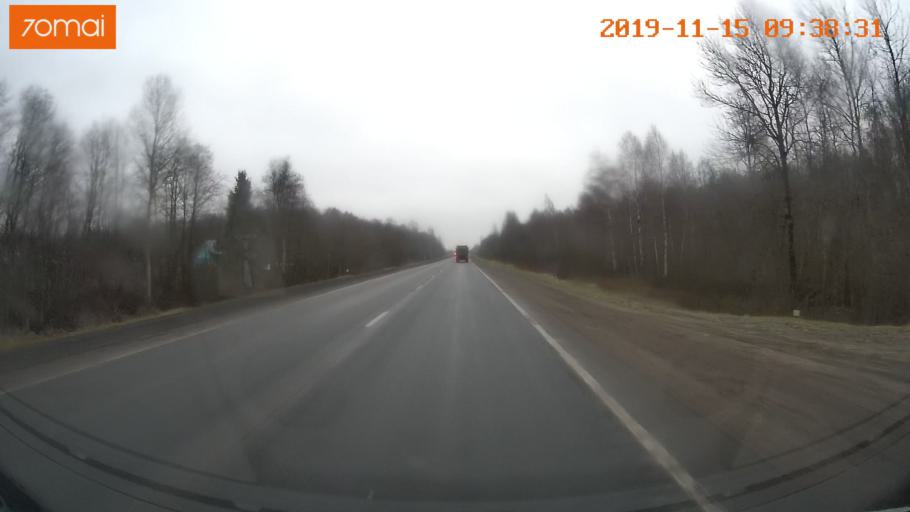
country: RU
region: Vologda
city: Sheksna
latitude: 59.2313
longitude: 38.4570
